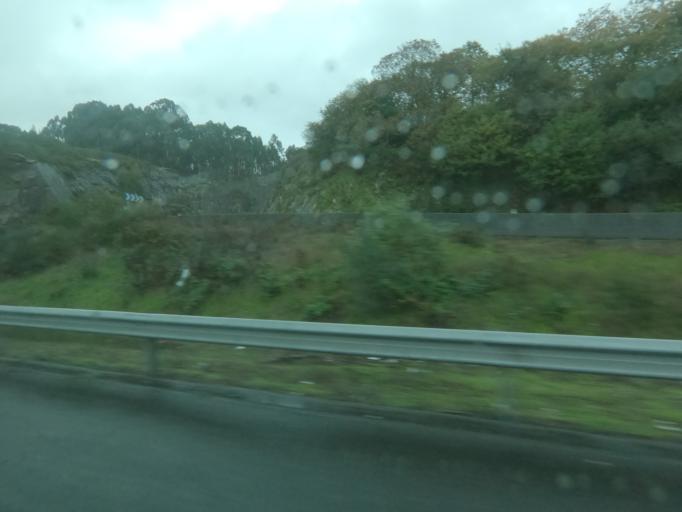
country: ES
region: Galicia
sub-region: Provincia de Pontevedra
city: Poio
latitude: 42.4152
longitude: -8.6528
